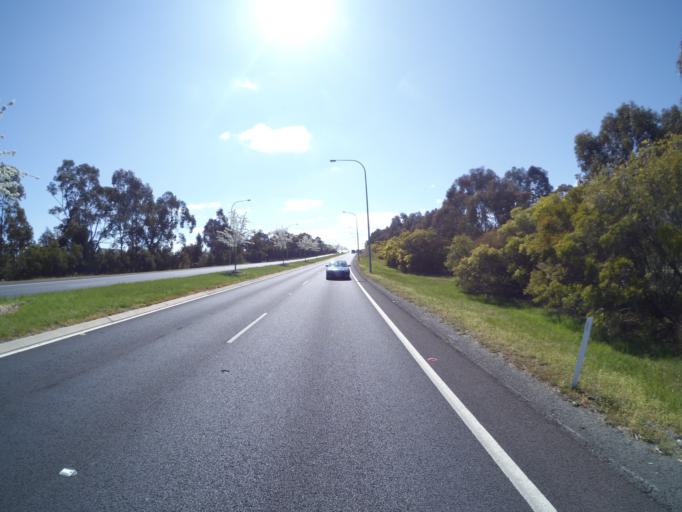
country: AU
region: New South Wales
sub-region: Queanbeyan
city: Queanbeyan
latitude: -35.3607
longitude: 149.2102
